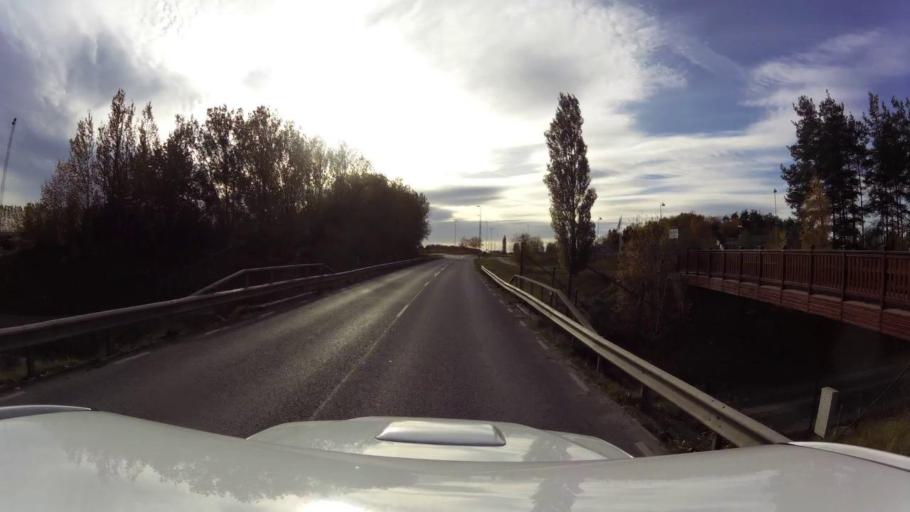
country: SE
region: OEstergoetland
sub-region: Linkopings Kommun
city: Ekangen
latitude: 58.4356
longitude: 15.6465
